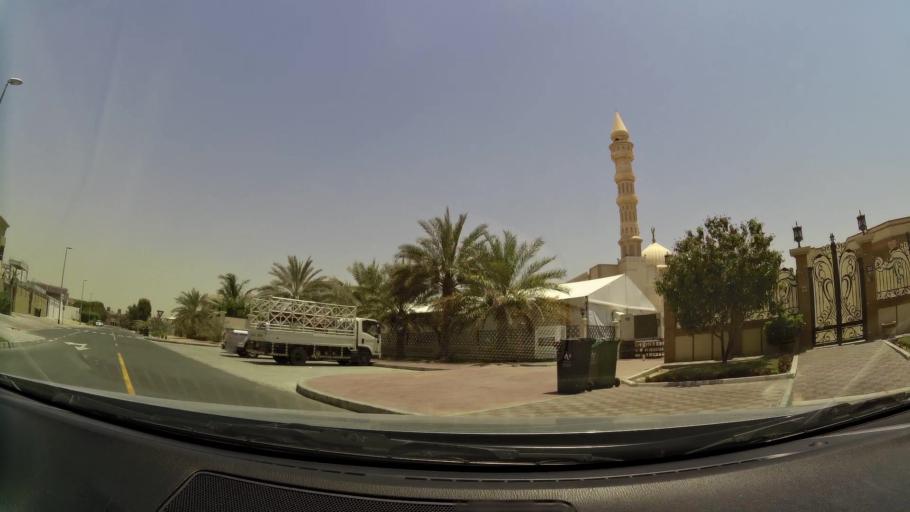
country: AE
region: Dubai
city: Dubai
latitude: 25.0978
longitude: 55.1960
